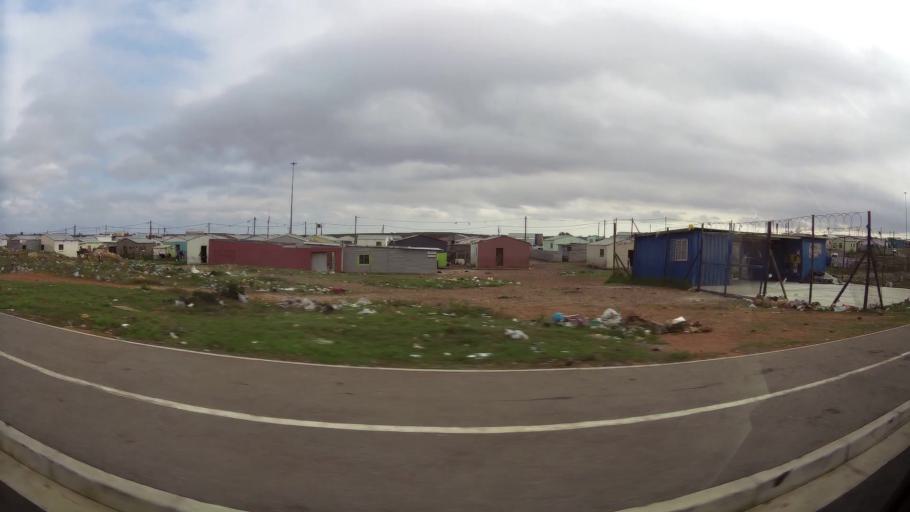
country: ZA
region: Eastern Cape
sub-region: Nelson Mandela Bay Metropolitan Municipality
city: Port Elizabeth
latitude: -33.9146
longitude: 25.5352
